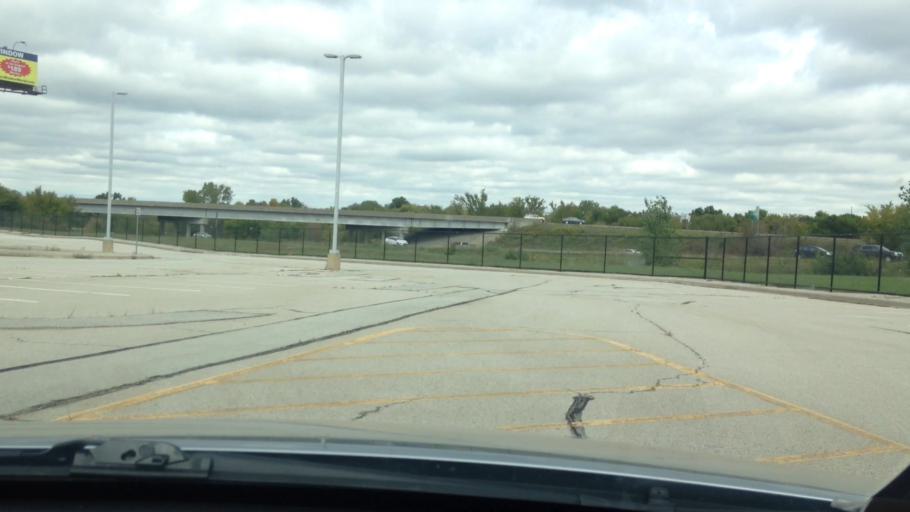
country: US
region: Missouri
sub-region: Platte County
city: Weatherby Lake
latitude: 39.3170
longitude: -94.6942
